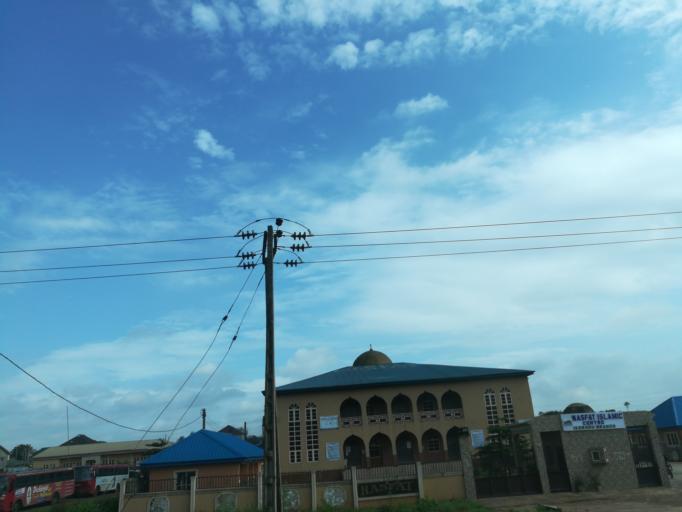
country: NG
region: Lagos
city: Ikorodu
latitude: 6.6309
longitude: 3.5237
